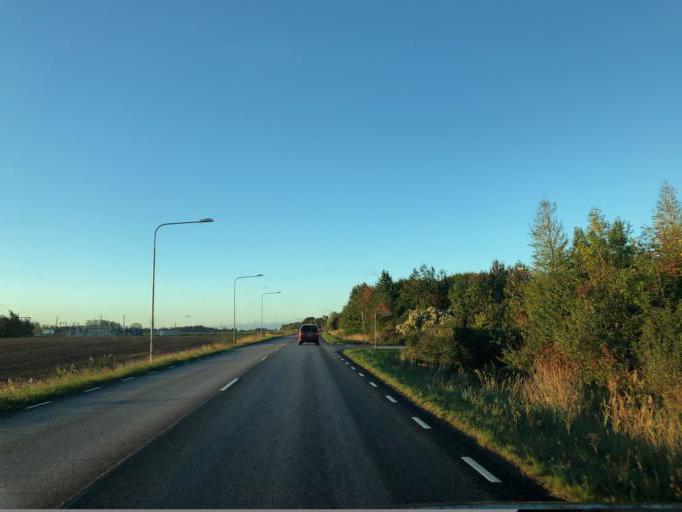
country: SE
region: Skane
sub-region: Lomma Kommun
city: Lomma
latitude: 55.6773
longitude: 13.0960
